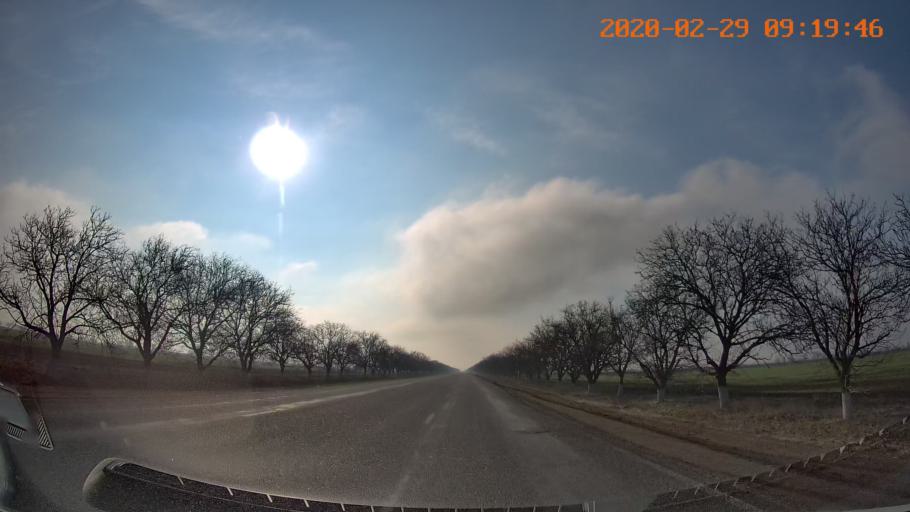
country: MD
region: Telenesti
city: Pervomaisc
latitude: 46.7584
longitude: 29.9421
